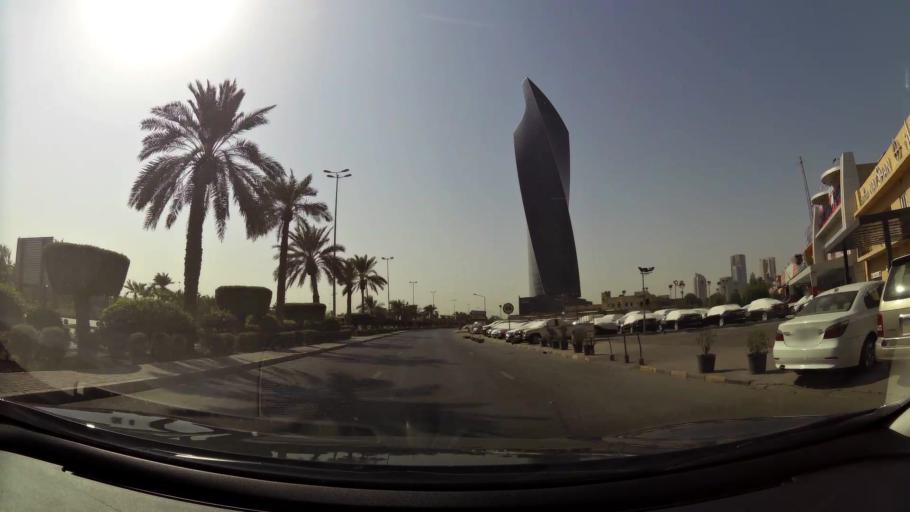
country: KW
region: Al Asimah
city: Ad Dasmah
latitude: 29.3733
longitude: 47.9938
